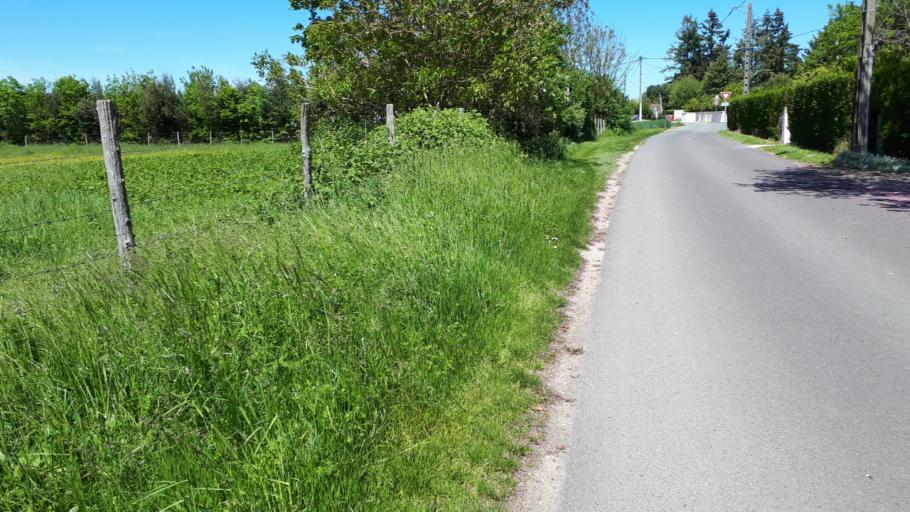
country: FR
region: Centre
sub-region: Departement du Loir-et-Cher
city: Villiers-sur-Loir
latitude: 47.7902
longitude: 0.9992
